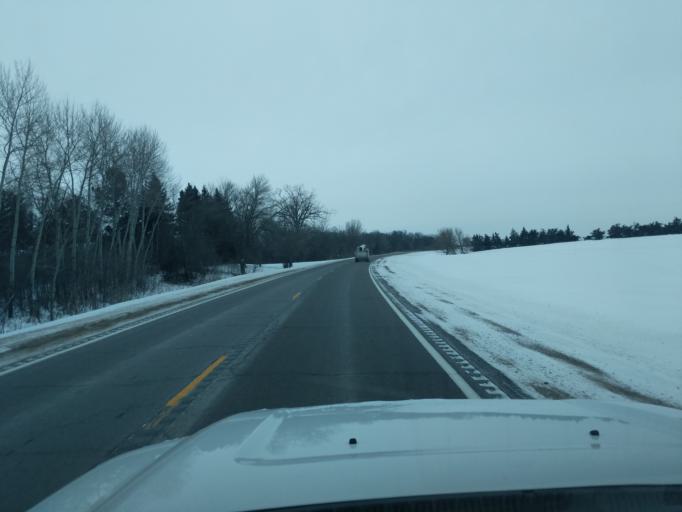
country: US
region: Minnesota
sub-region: Redwood County
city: Redwood Falls
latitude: 44.5692
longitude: -94.9947
